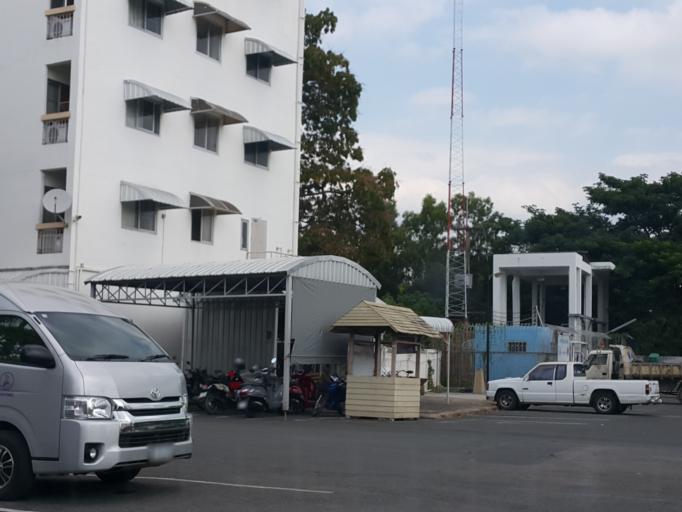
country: TH
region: Chiang Mai
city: Chiang Mai
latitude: 18.8045
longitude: 98.9932
